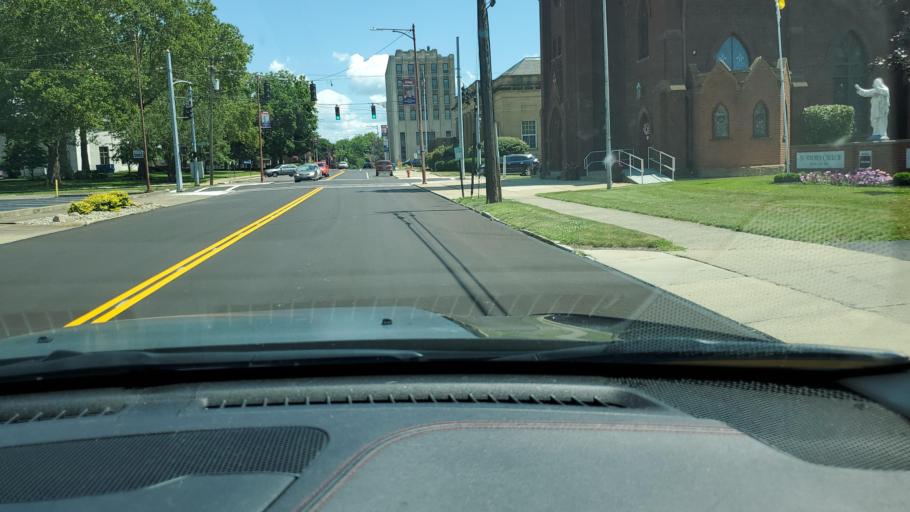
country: US
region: Ohio
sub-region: Trumbull County
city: Niles
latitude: 41.1804
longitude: -80.7675
